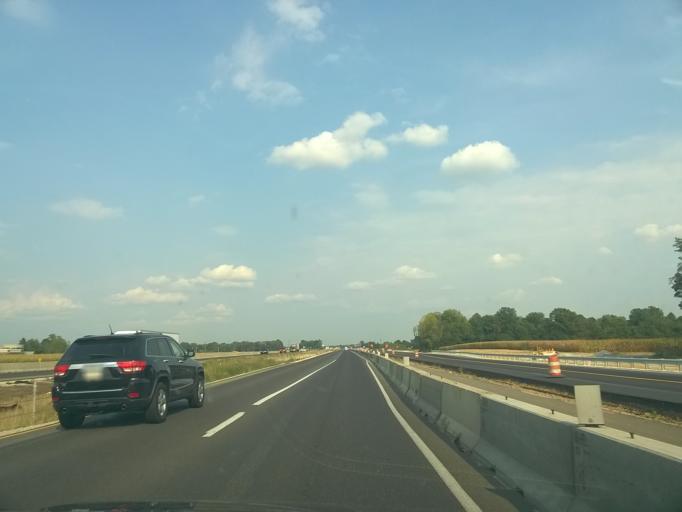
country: US
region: Indiana
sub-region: Vigo County
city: Terre Haute
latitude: 39.4305
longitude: -87.3348
